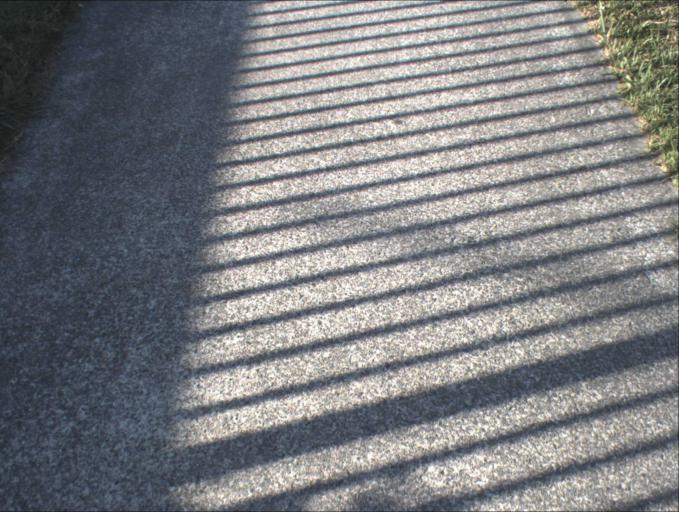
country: AU
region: Queensland
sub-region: Gold Coast
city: Yatala
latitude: -27.7082
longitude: 153.2203
